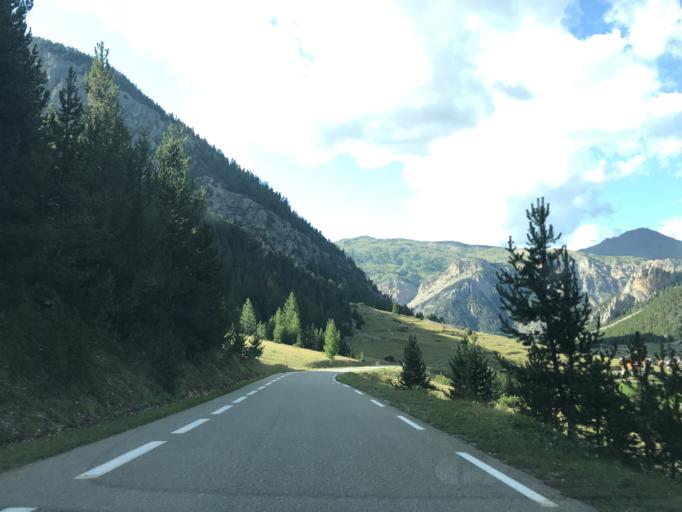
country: IT
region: Piedmont
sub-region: Provincia di Torino
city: Claviere
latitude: 44.8507
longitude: 6.7249
